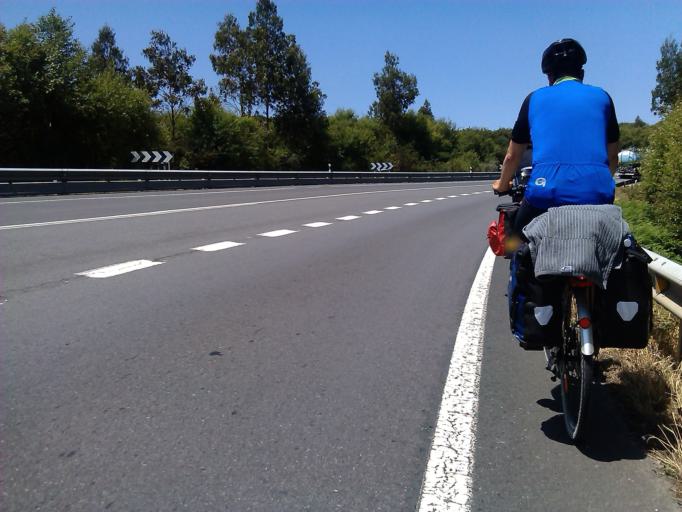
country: ES
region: Galicia
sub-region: Provincia da Coruna
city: Oroso
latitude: 42.9083
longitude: -8.4046
